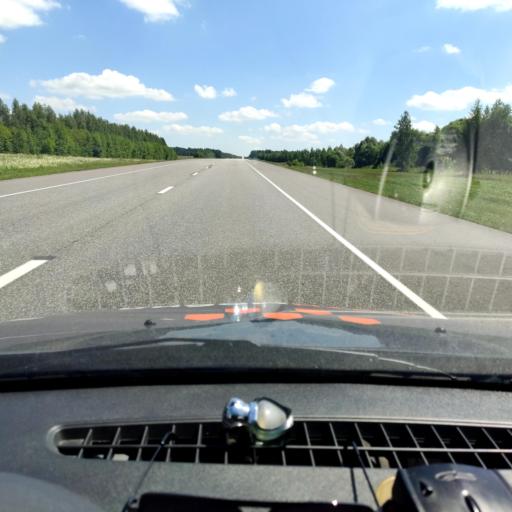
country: RU
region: Orjol
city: Zmiyevka
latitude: 52.8134
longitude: 36.2885
